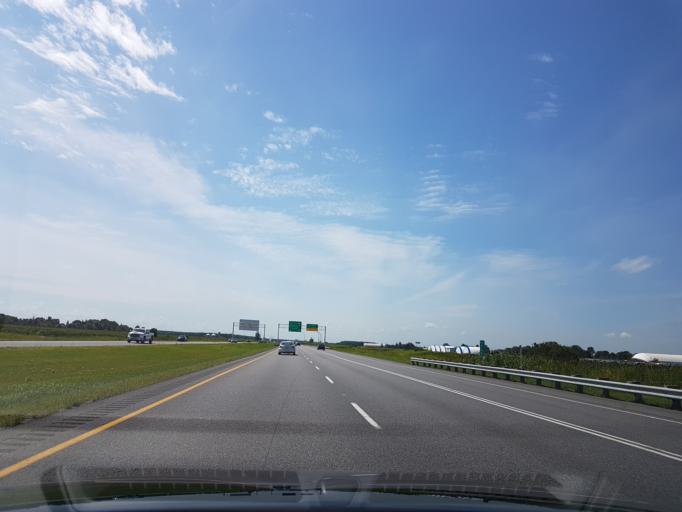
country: CA
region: Quebec
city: Les Cedres
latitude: 45.3457
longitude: -74.0755
